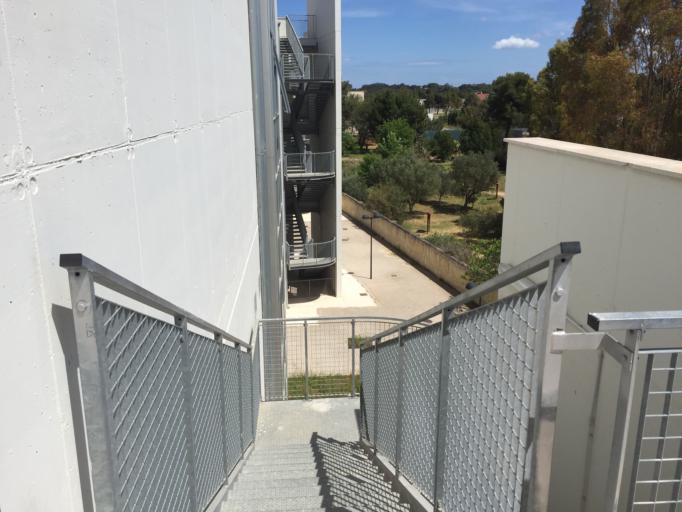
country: IT
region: Apulia
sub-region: Provincia di Lecce
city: San Pietro in Lama
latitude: 40.3357
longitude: 18.1221
